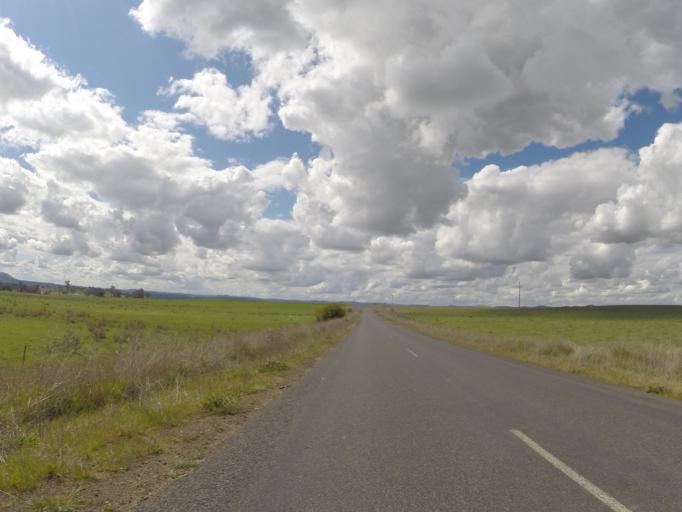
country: AU
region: New South Wales
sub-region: Yass Valley
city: Yass
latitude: -34.9024
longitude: 148.8901
